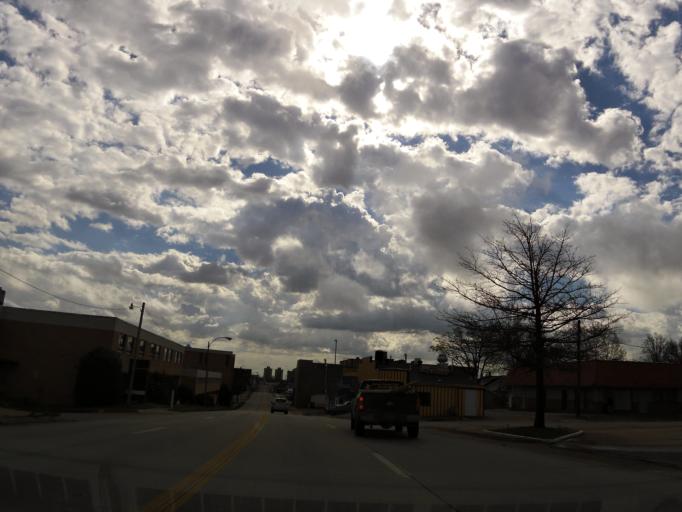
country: US
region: Missouri
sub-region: Butler County
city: Poplar Bluff
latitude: 36.7580
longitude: -90.3990
